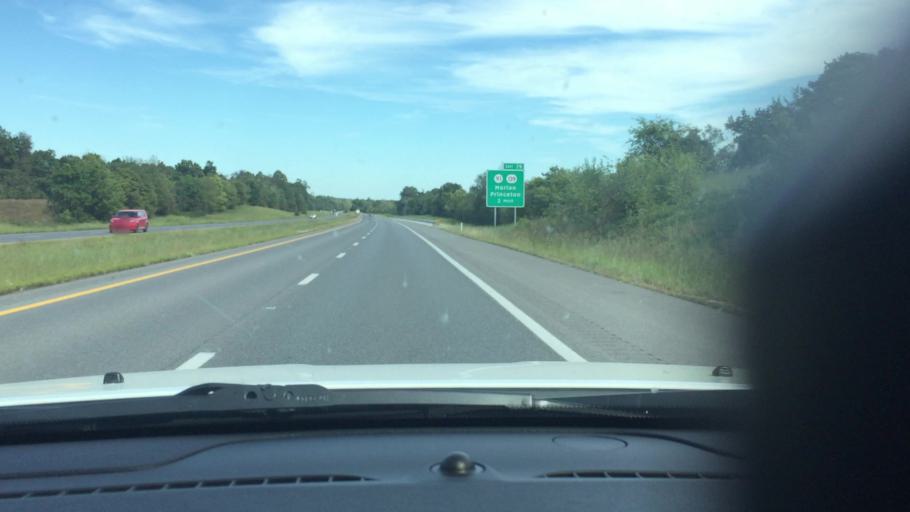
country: US
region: Kentucky
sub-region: Caldwell County
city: Princeton
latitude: 37.1131
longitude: -87.9350
